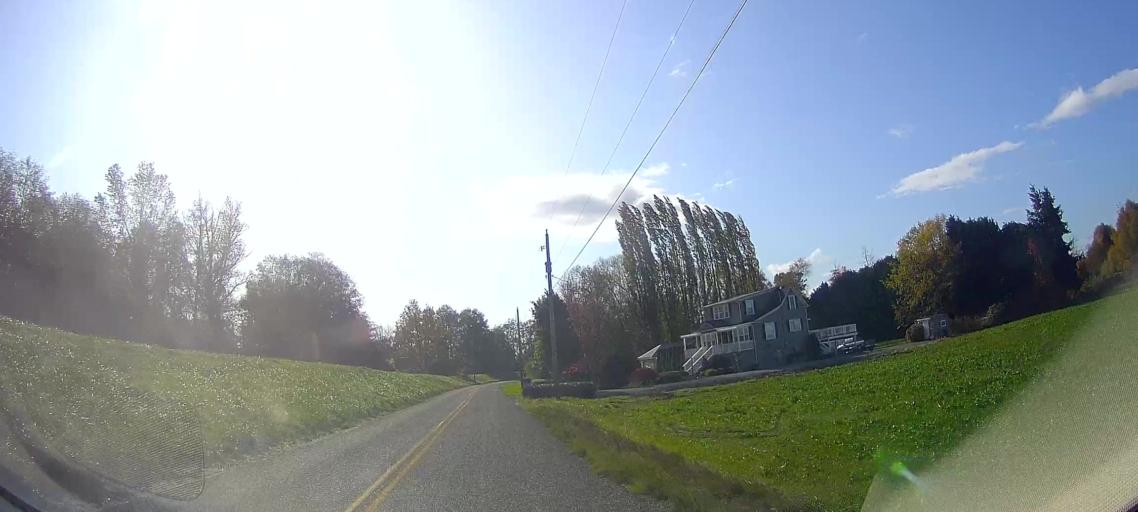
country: US
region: Washington
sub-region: Snohomish County
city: Stanwood
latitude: 48.3299
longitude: -122.3532
